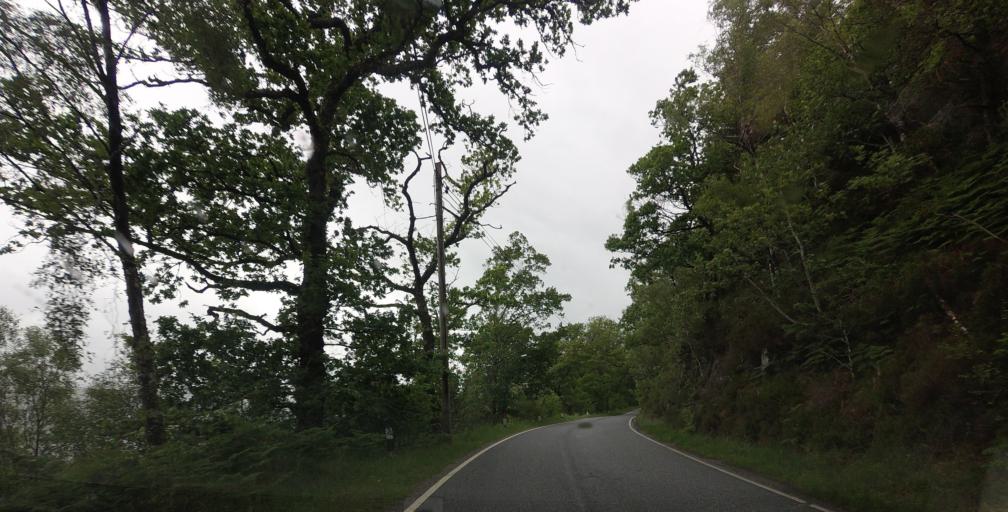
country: GB
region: Scotland
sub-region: Argyll and Bute
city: Isle Of Mull
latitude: 56.7115
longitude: -5.7638
